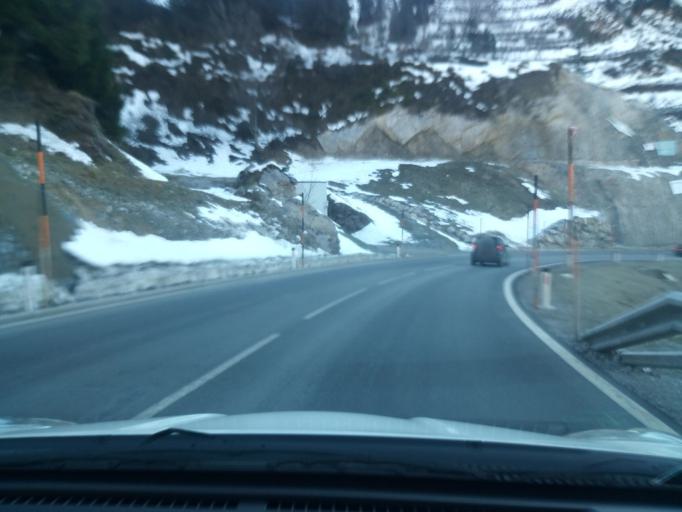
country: AT
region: Vorarlberg
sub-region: Politischer Bezirk Bludenz
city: Lech
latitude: 47.1390
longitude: 10.1639
